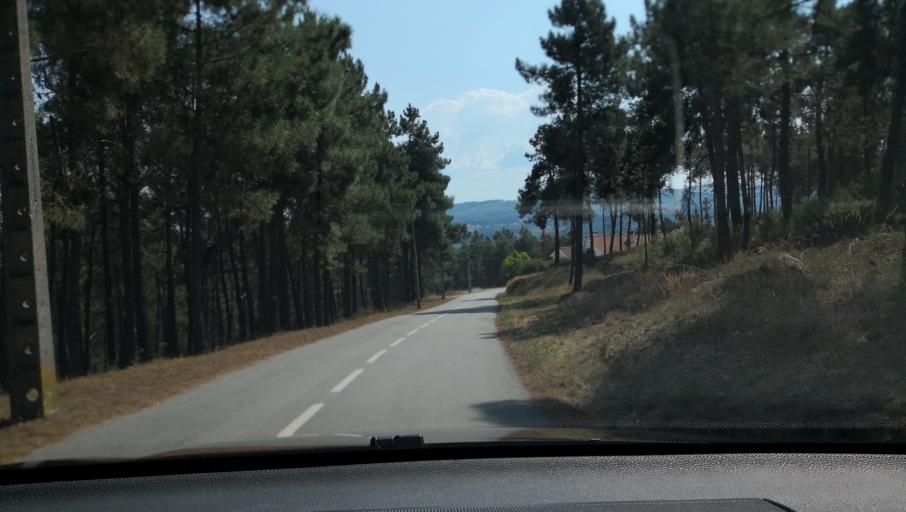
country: PT
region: Vila Real
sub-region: Sabrosa
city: Sabrosa
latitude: 41.2745
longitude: -7.6180
